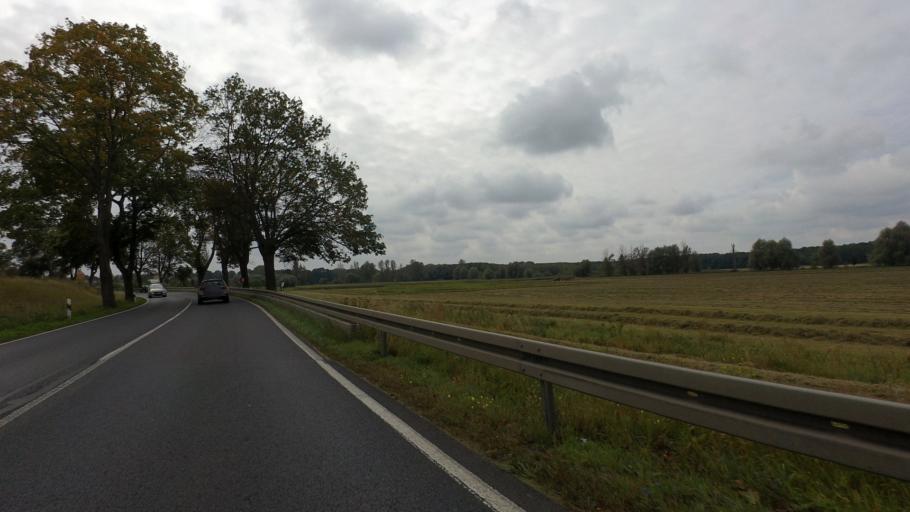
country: DE
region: Brandenburg
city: Rangsdorf
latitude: 52.2803
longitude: 13.4630
